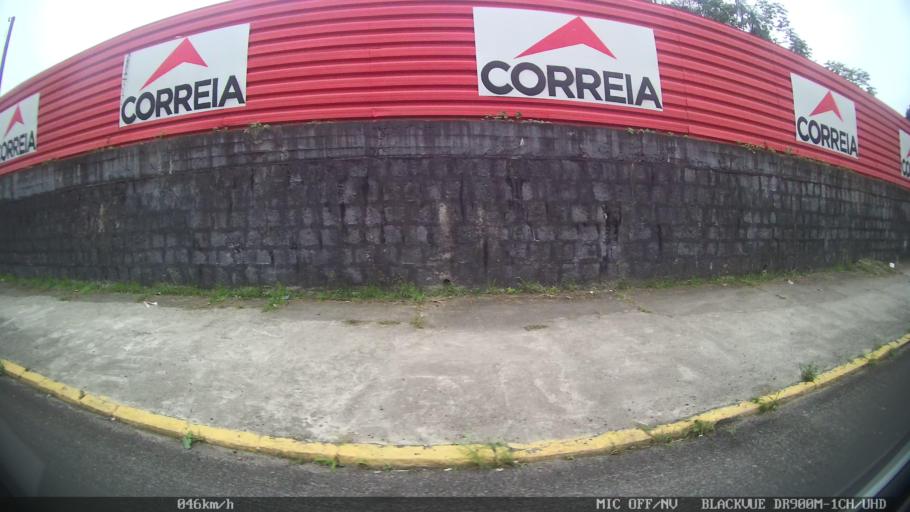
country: BR
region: Santa Catarina
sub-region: Joinville
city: Joinville
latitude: -26.3182
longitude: -48.8573
